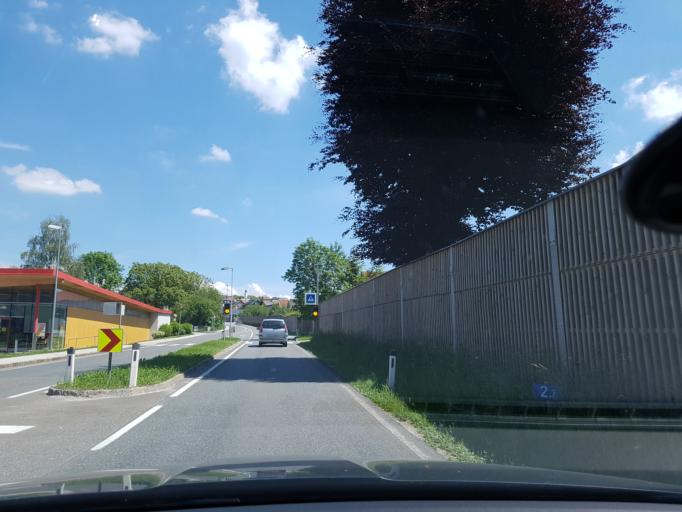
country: AT
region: Salzburg
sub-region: Politischer Bezirk Salzburg-Umgebung
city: Elixhausen
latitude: 47.8611
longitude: 13.0603
